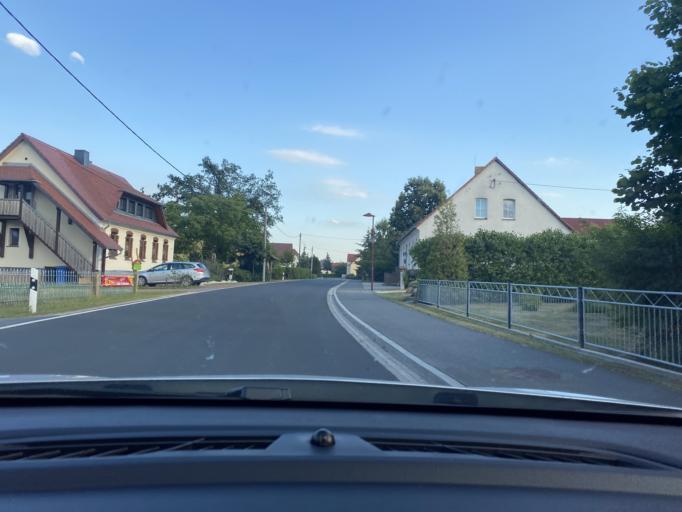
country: DE
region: Saxony
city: Kodersdorf
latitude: 51.2600
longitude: 14.8871
